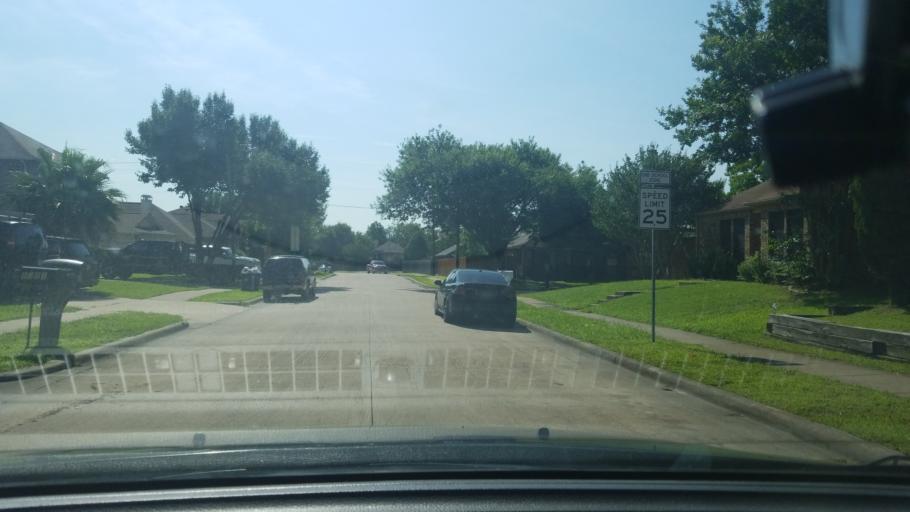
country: US
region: Texas
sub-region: Dallas County
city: Mesquite
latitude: 32.7739
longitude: -96.5790
